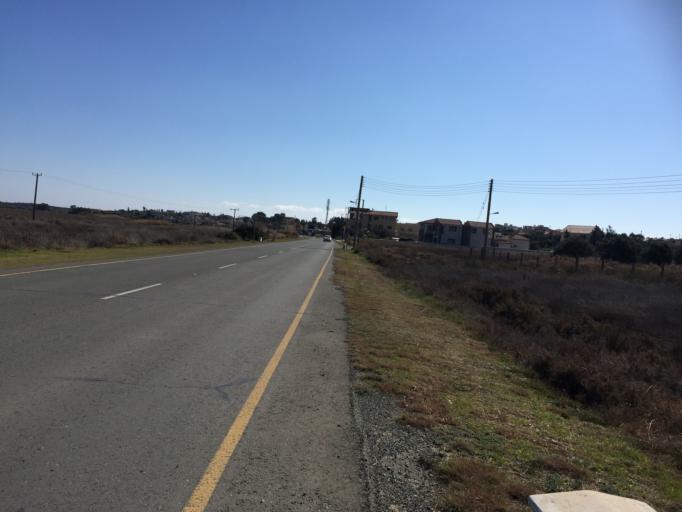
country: CY
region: Larnaka
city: Kolossi
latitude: 34.6072
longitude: 32.9491
